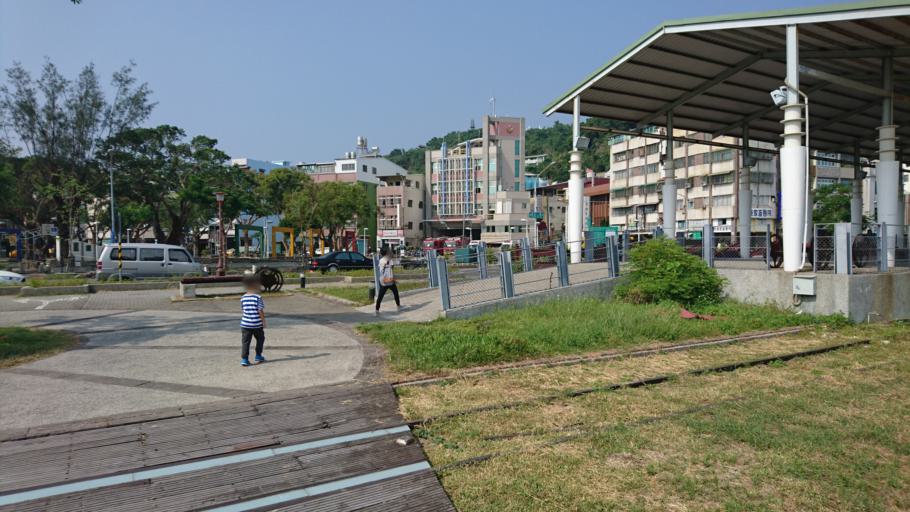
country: TW
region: Kaohsiung
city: Kaohsiung
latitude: 22.6226
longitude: 120.2761
